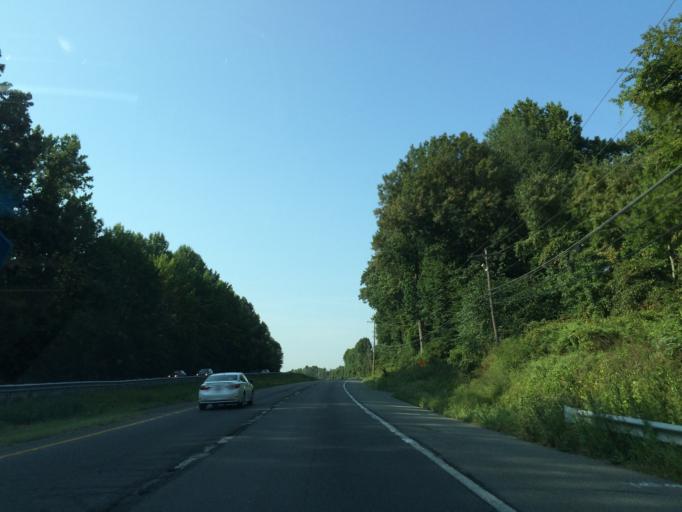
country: US
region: Maryland
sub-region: Prince George's County
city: Marlboro Meadows
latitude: 38.8402
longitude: -76.7281
